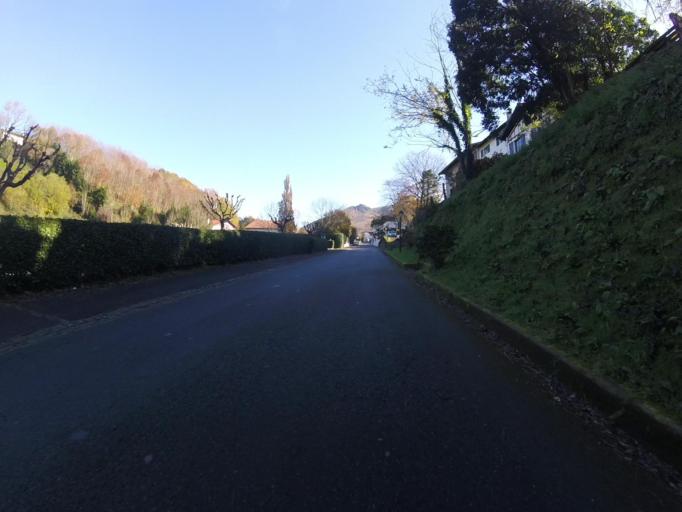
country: ES
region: Basque Country
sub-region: Provincia de Guipuzcoa
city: Irun
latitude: 43.3338
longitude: -1.7459
